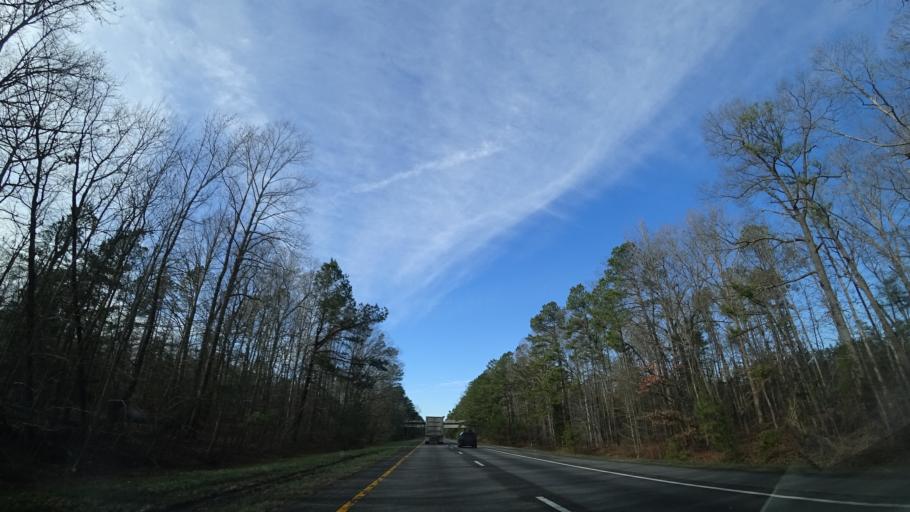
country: US
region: Virginia
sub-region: New Kent County
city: New Kent
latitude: 37.5028
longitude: -77.0821
